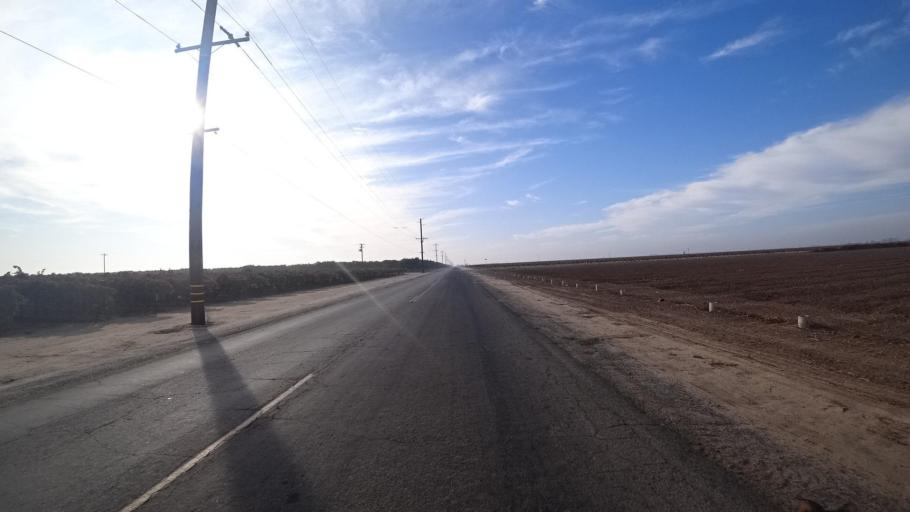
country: US
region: California
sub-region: Kern County
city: Delano
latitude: 35.7335
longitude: -119.2052
